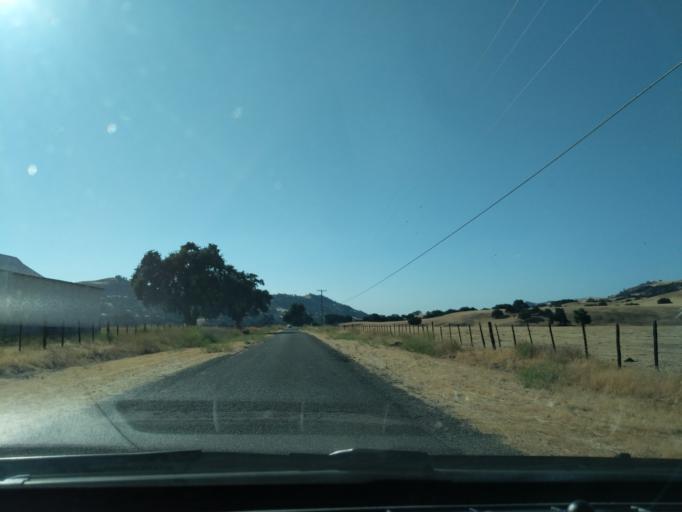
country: US
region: California
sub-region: San Luis Obispo County
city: San Miguel
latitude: 36.1136
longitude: -120.7230
